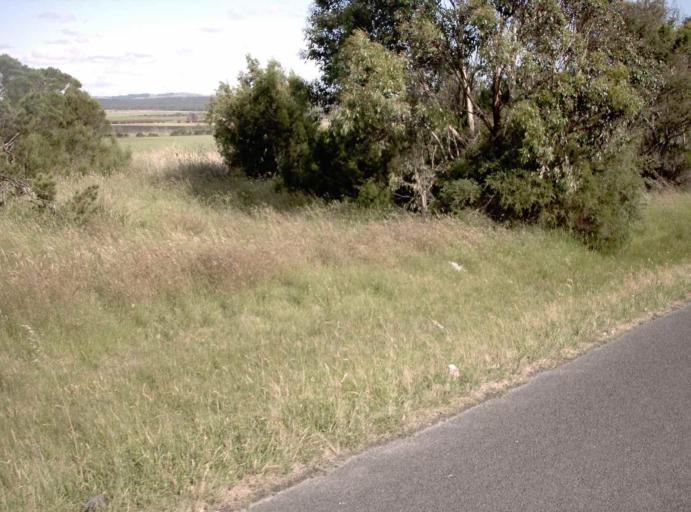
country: AU
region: Victoria
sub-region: Cardinia
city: Koo-Wee-Rup
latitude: -38.3189
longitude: 145.5399
